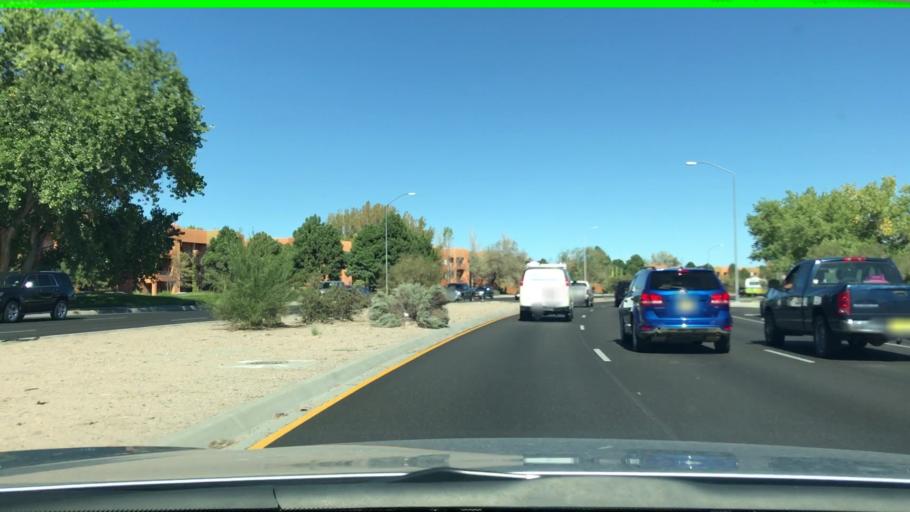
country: US
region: New Mexico
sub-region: Sandoval County
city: Rio Rancho
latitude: 35.1974
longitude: -106.6603
